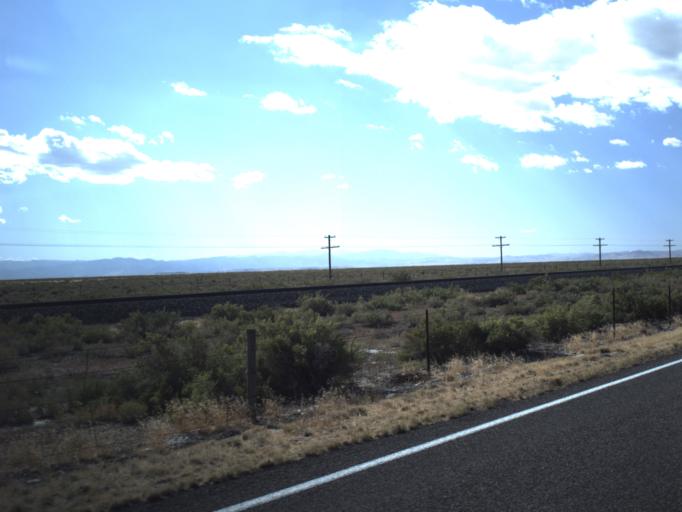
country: US
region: Utah
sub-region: Millard County
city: Delta
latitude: 39.0987
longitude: -112.7482
